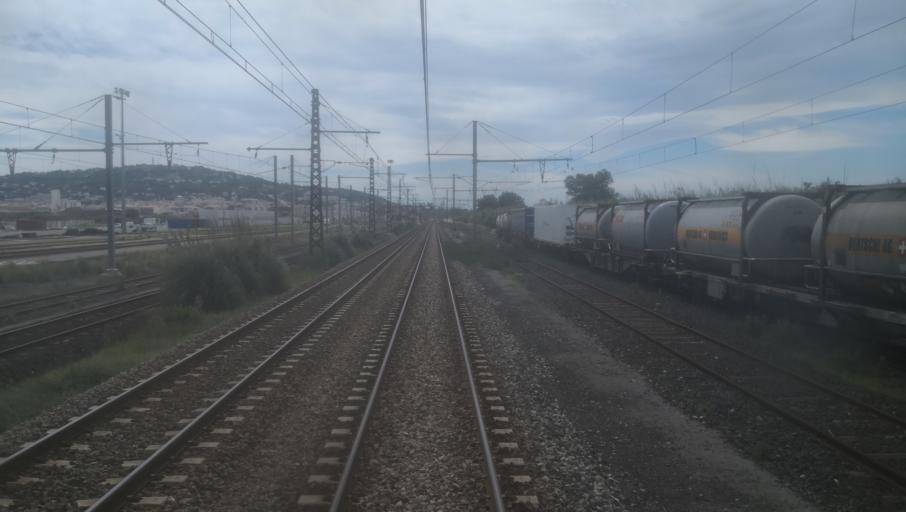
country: FR
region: Languedoc-Roussillon
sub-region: Departement de l'Herault
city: Sete
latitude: 43.4160
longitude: 3.7119
